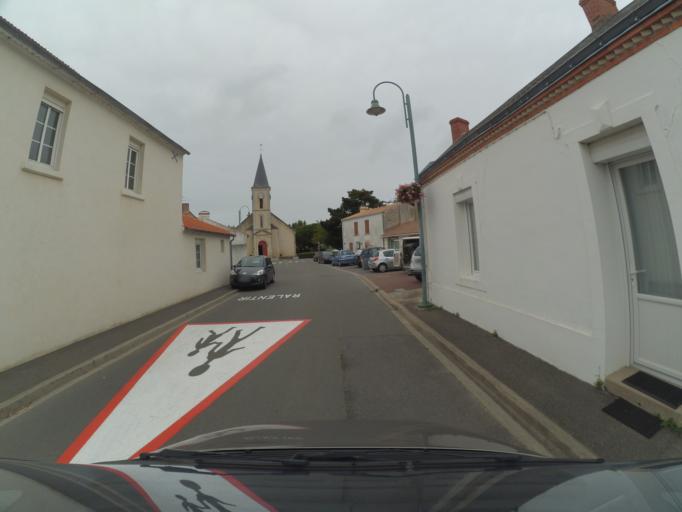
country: FR
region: Pays de la Loire
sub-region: Departement de la Vendee
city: La Barre-de-Monts
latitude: 46.8839
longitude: -2.1180
